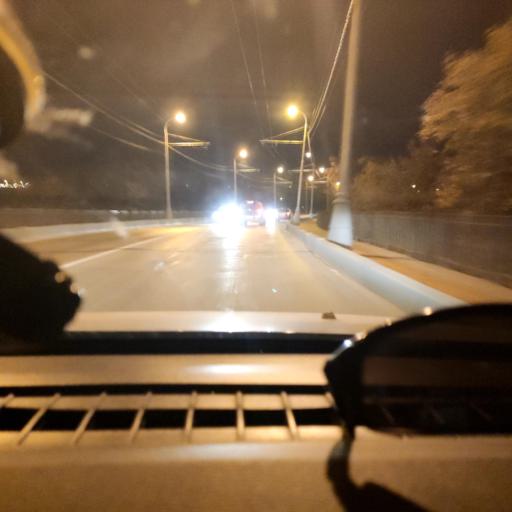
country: RU
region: Samara
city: Rozhdestveno
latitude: 53.1711
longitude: 50.0754
